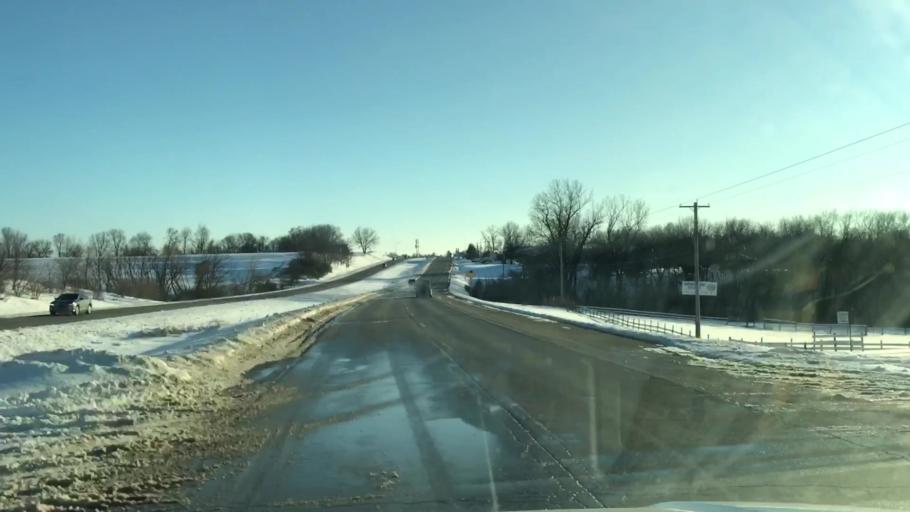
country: US
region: Missouri
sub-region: Andrew County
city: Country Club Village
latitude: 39.8650
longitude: -94.8086
